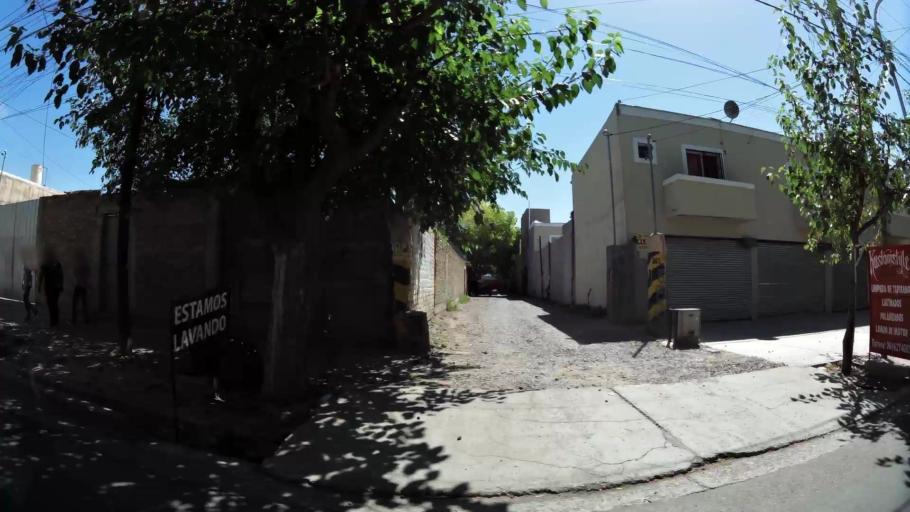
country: AR
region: Mendoza
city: Villa Nueva
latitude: -32.8967
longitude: -68.7908
